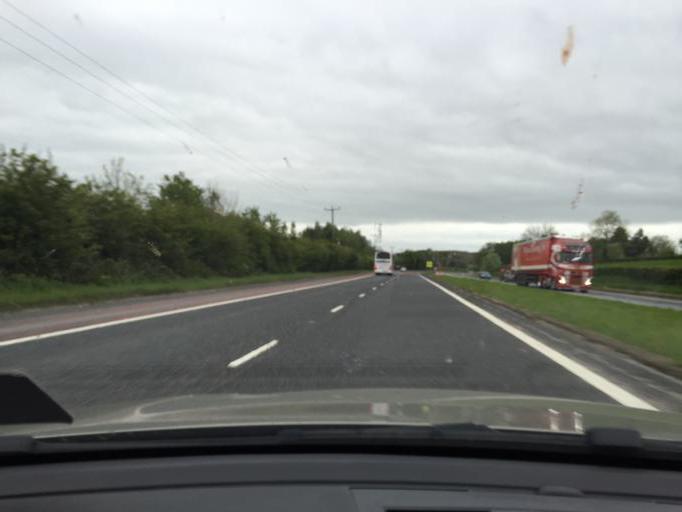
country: GB
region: Northern Ireland
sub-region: Banbridge District
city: Banbridge
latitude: 54.3636
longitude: -6.2240
